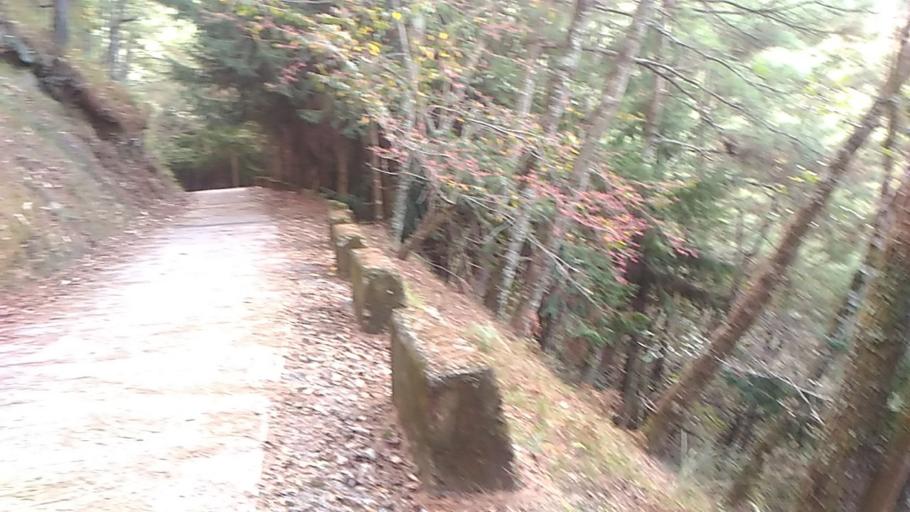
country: TW
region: Taiwan
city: Daxi
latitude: 24.4036
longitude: 121.3069
